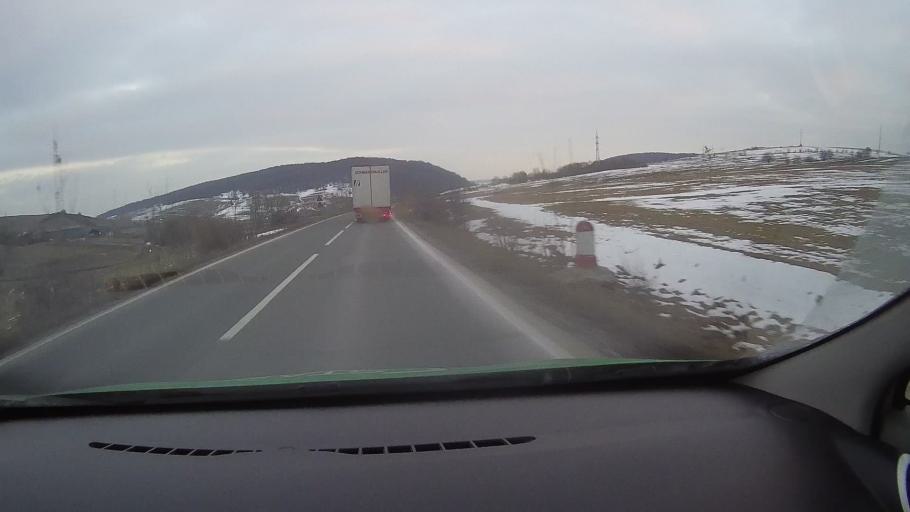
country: RO
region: Harghita
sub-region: Municipiul Odorheiu Secuiesc
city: Odorheiu Secuiesc
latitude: 46.3451
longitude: 25.2657
